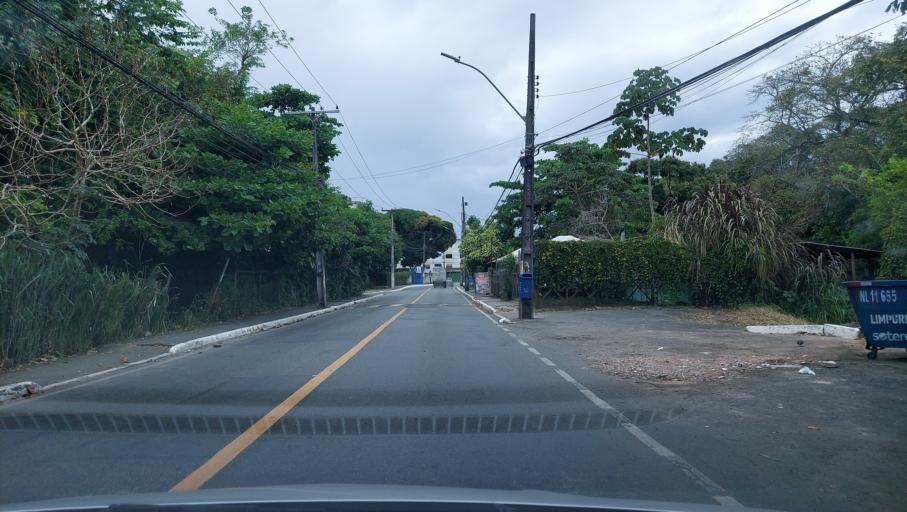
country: BR
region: Bahia
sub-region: Salvador
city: Salvador
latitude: -12.9642
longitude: -38.4437
